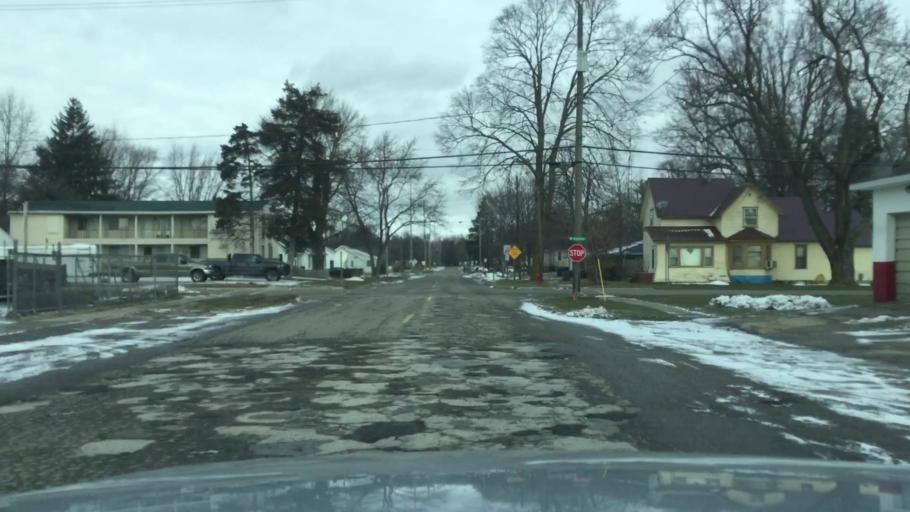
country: US
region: Michigan
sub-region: Genesee County
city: Montrose
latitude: 43.1766
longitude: -83.8943
